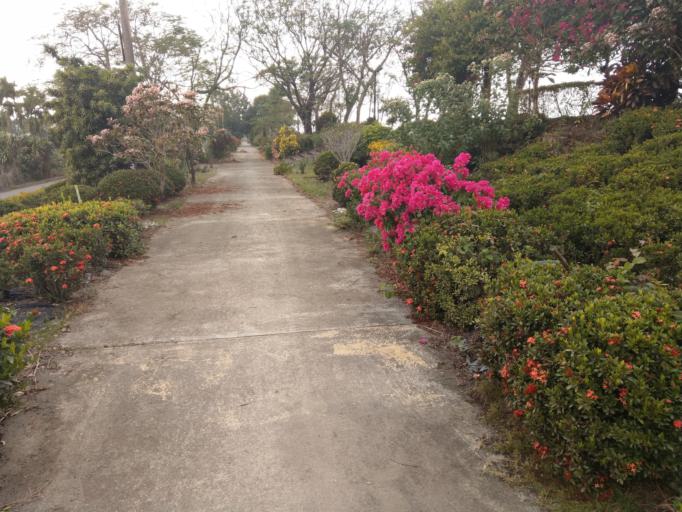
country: TW
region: Taiwan
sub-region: Pingtung
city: Pingtung
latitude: 22.7821
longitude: 120.5390
